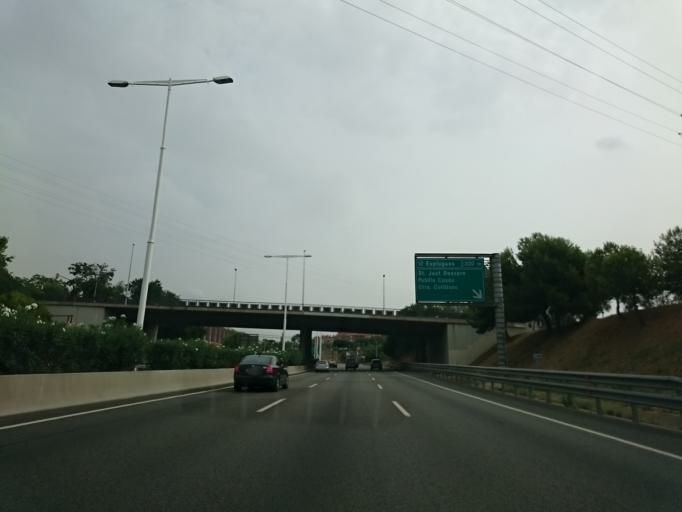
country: ES
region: Catalonia
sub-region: Provincia de Barcelona
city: Esplugues de Llobregat
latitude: 41.3698
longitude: 2.0921
